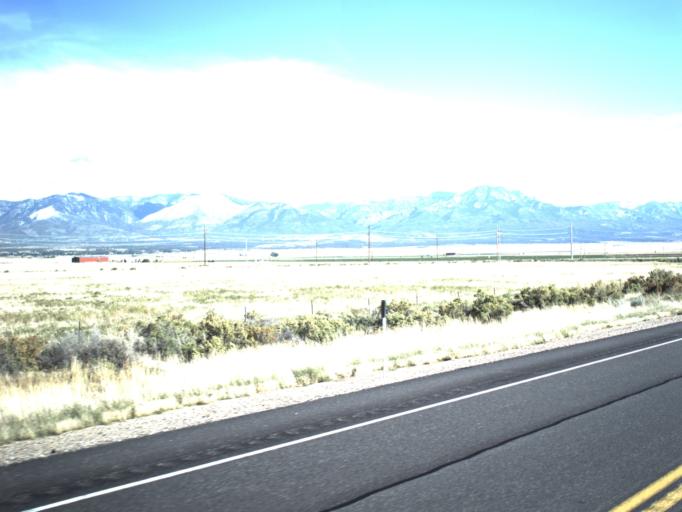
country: US
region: Utah
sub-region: Millard County
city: Fillmore
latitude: 39.1219
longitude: -112.3572
